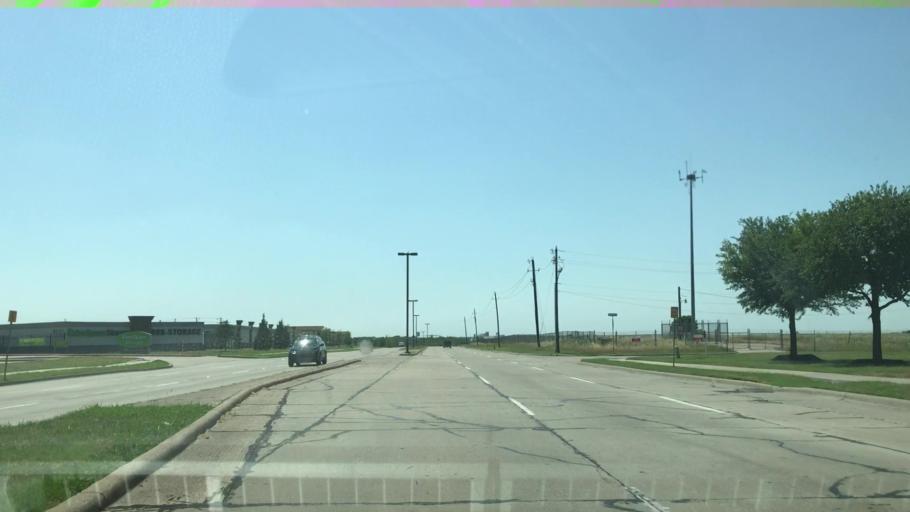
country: US
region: Texas
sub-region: Dallas County
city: Irving
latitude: 32.8662
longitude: -97.0044
